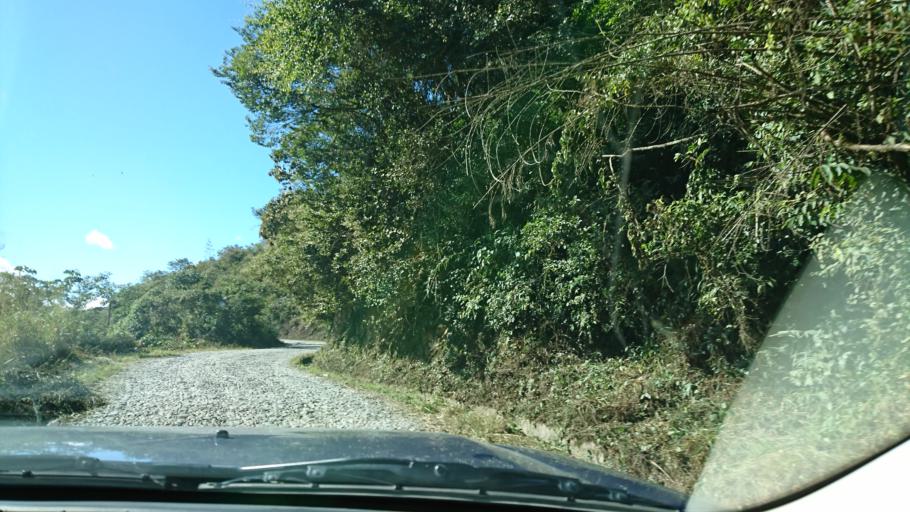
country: BO
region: La Paz
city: Coroico
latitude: -16.2170
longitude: -67.7371
